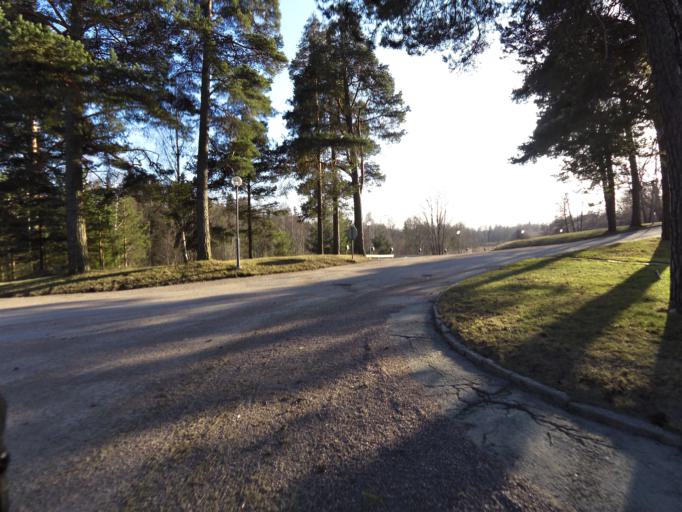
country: SE
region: Gaevleborg
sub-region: Gavle Kommun
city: Gavle
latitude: 60.6858
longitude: 17.2299
